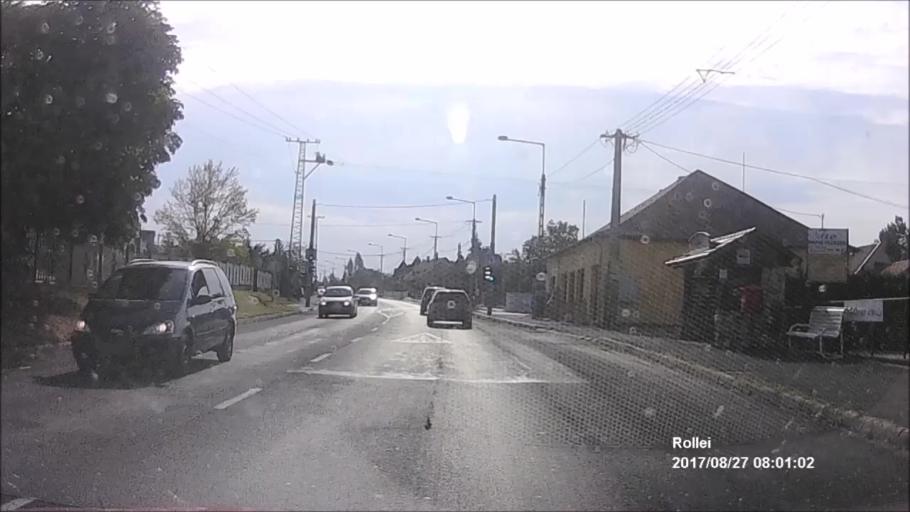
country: HU
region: Zala
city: Vonyarcvashegy
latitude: 46.7633
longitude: 17.3079
